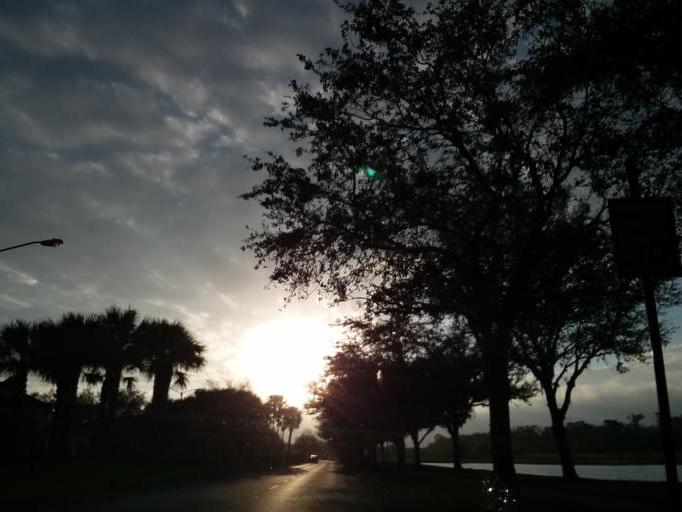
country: US
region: Florida
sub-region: Osceola County
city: Campbell
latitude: 28.2275
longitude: -81.4477
